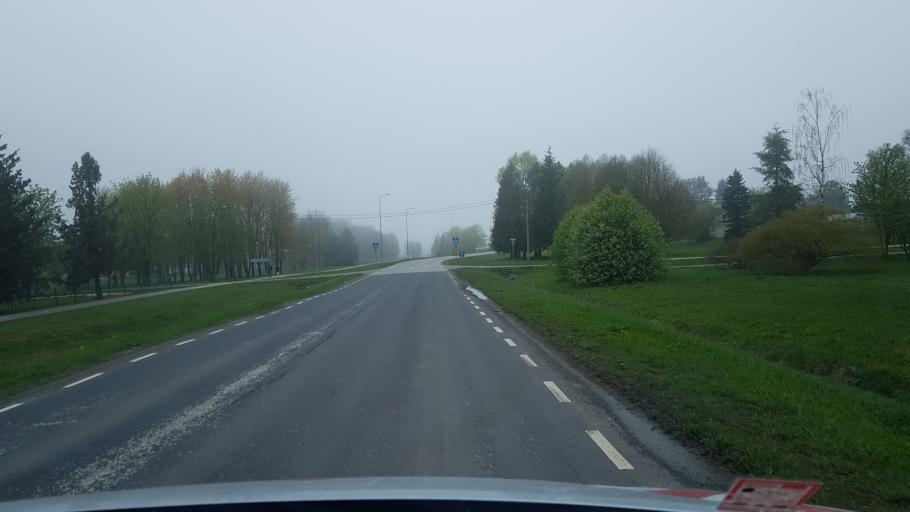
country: EE
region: Harju
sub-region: Joelaehtme vald
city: Loo
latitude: 59.4315
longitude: 24.9403
